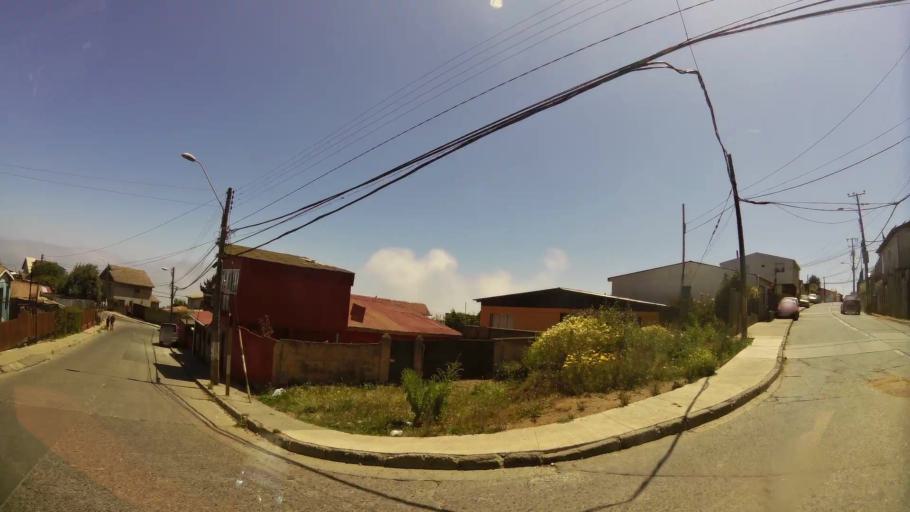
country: CL
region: Valparaiso
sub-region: Provincia de Valparaiso
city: Valparaiso
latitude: -33.0354
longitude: -71.6510
